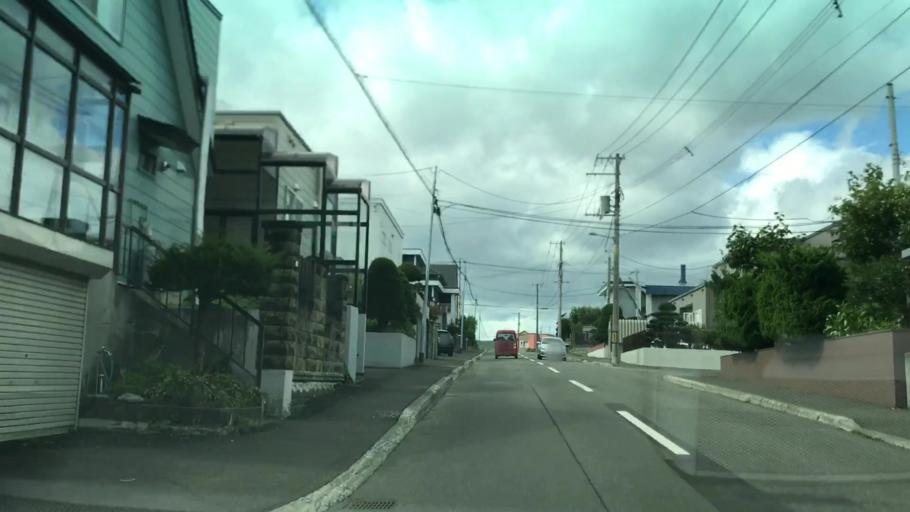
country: JP
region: Hokkaido
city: Kitahiroshima
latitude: 42.9858
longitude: 141.4447
